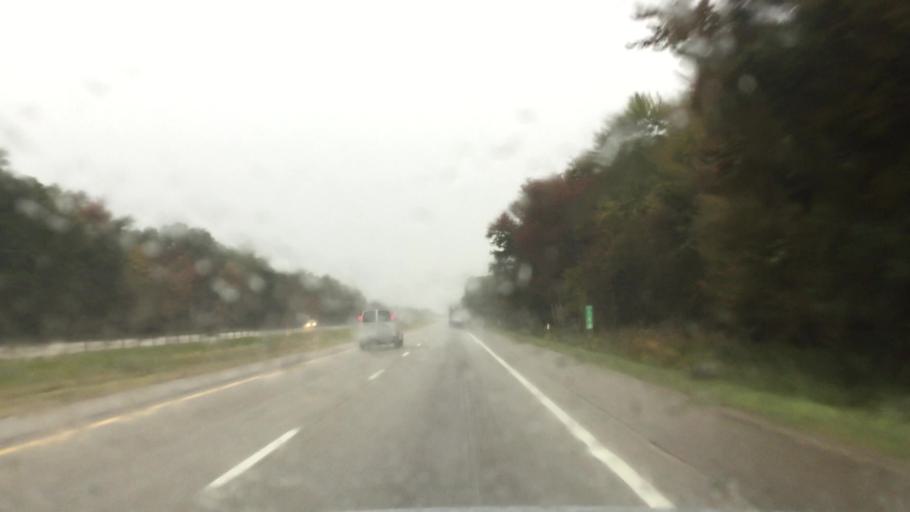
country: US
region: Michigan
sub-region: Van Buren County
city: Mattawan
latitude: 42.2213
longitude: -85.8090
